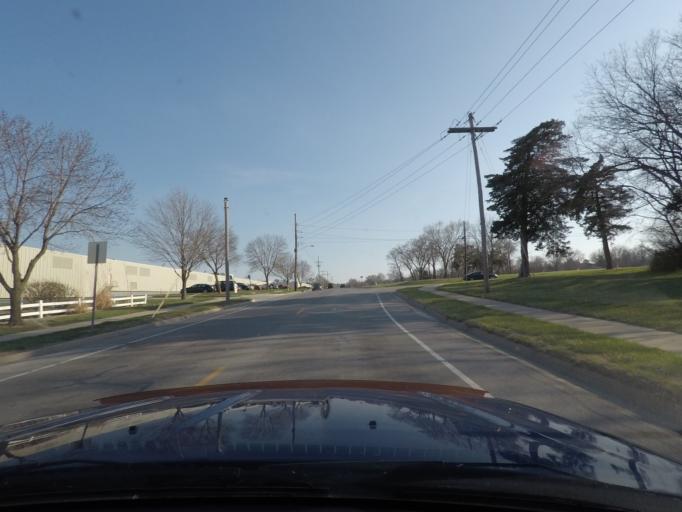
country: US
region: Kansas
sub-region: Douglas County
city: Lawrence
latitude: 38.9866
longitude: -95.2604
